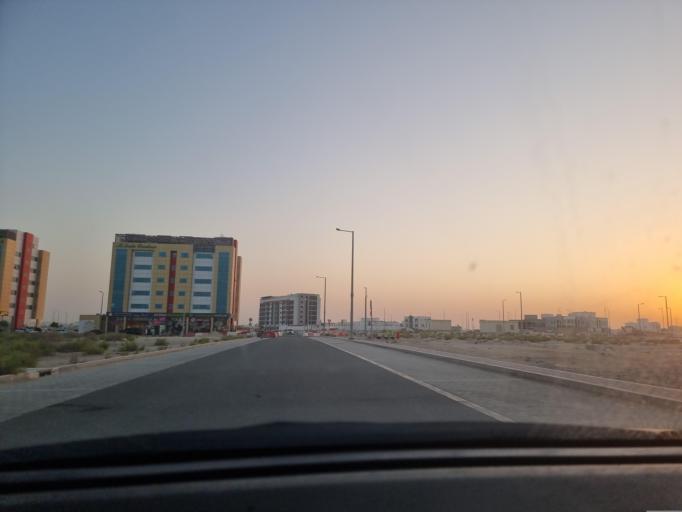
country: AE
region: Abu Dhabi
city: Abu Dhabi
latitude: 24.3696
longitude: 54.7405
